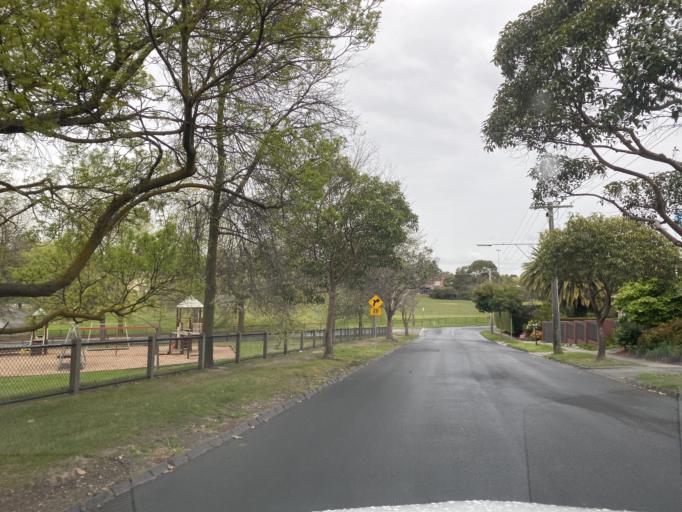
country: AU
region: Victoria
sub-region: Boroondara
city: Camberwell
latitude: -37.8425
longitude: 145.0857
